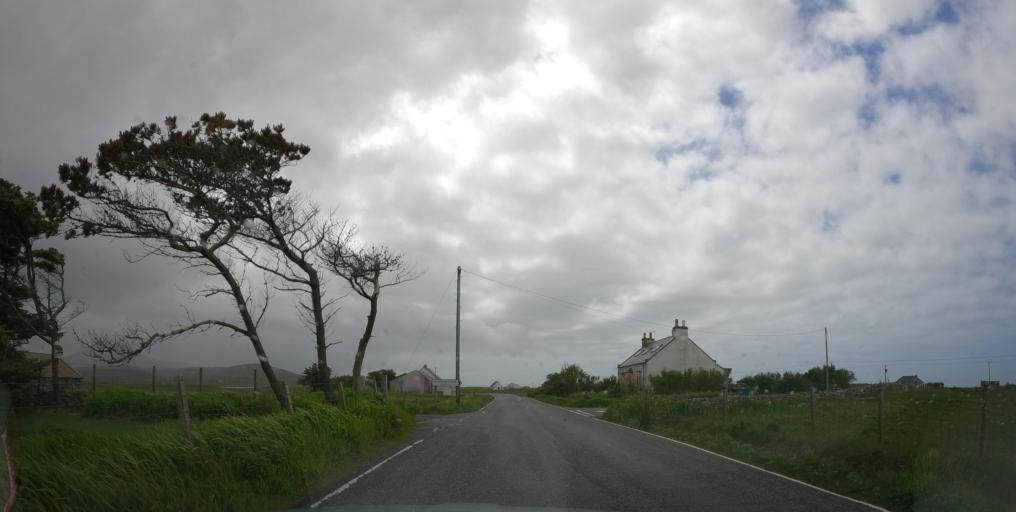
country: GB
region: Scotland
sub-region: Eilean Siar
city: Isle of South Uist
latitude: 57.3241
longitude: -7.3675
